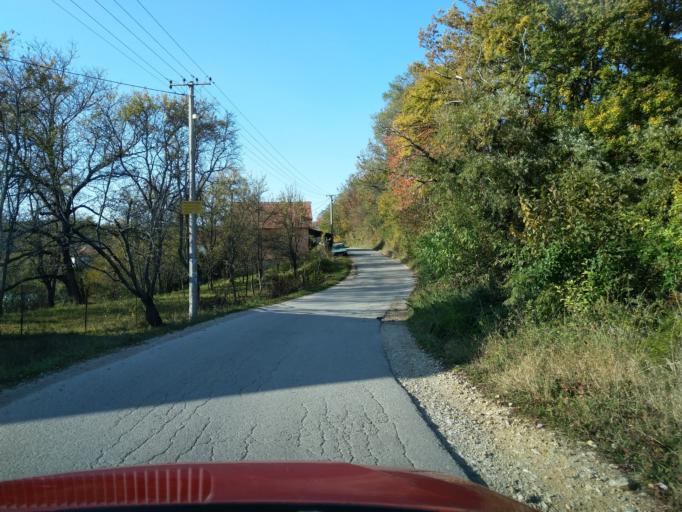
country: RS
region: Central Serbia
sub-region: Zlatiborski Okrug
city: Uzice
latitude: 43.8689
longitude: 19.7584
